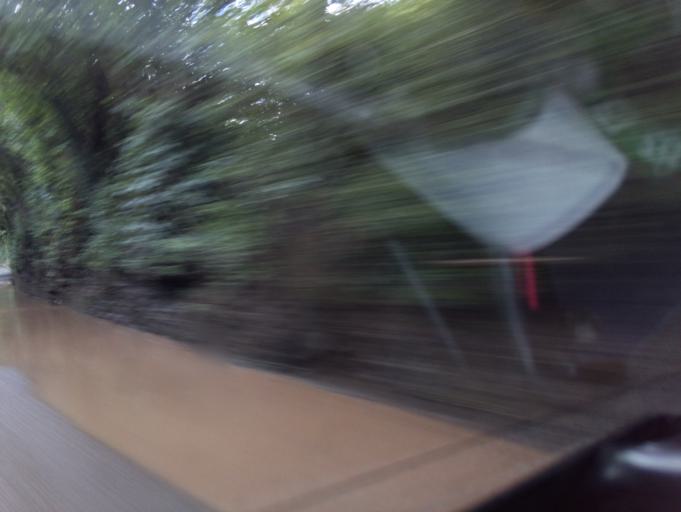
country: GB
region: England
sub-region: Devon
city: Modbury
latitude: 50.3324
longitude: -3.8476
